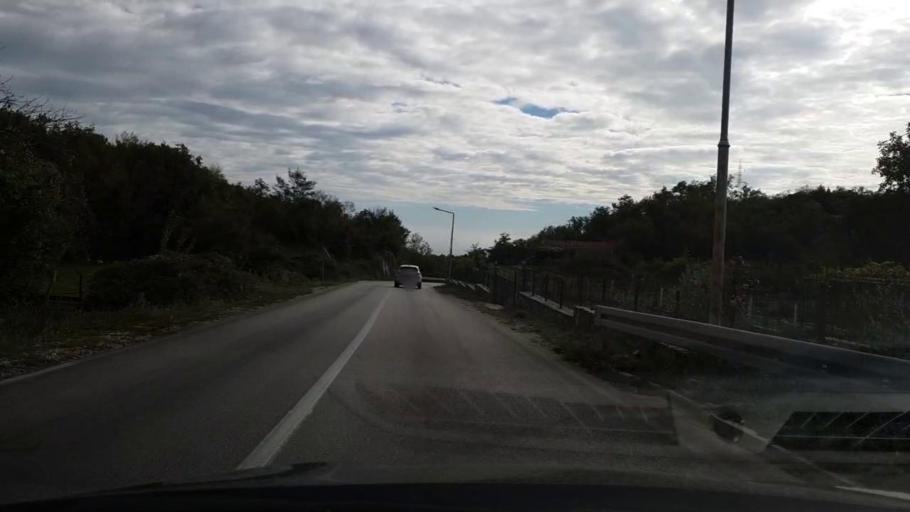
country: ME
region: Herceg Novi
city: Herceg-Novi
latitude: 42.4775
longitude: 18.5293
